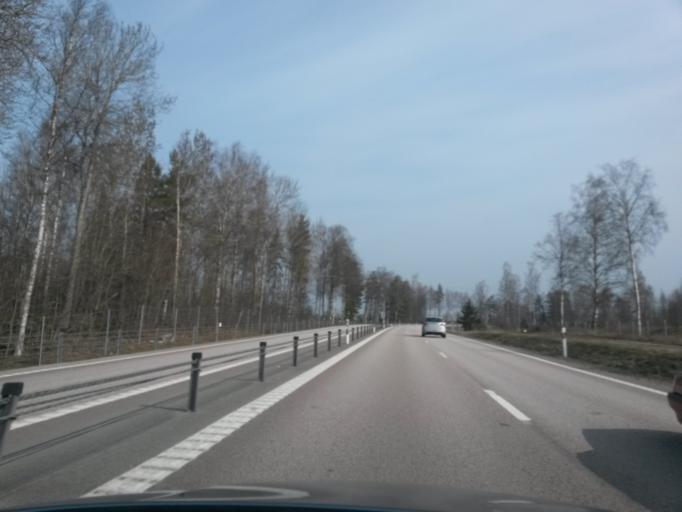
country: SE
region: Vaestra Goetaland
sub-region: Mariestads Kommun
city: Mariestad
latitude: 58.7605
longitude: 13.9704
